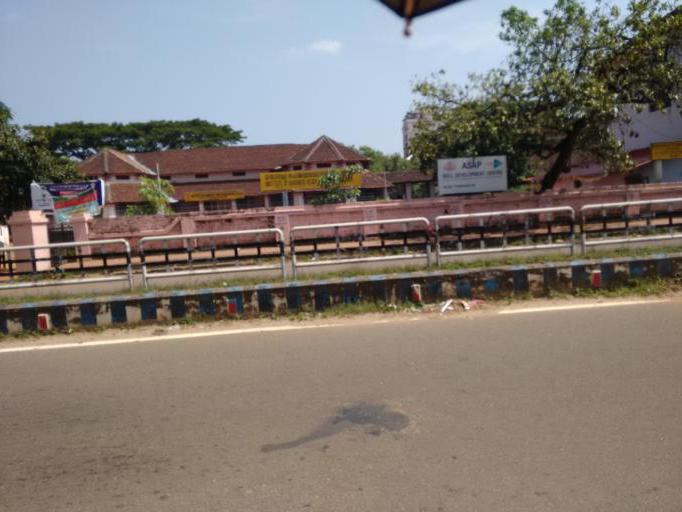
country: IN
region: Kerala
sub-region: Thrissur District
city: Trichur
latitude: 10.5275
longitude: 76.2181
